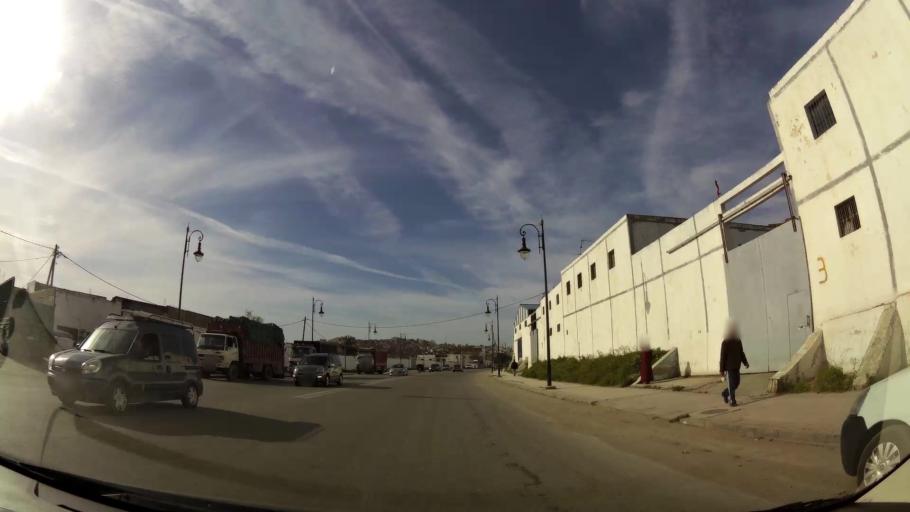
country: MA
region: Tanger-Tetouan
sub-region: Tanger-Assilah
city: Tangier
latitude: 35.7635
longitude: -5.7830
